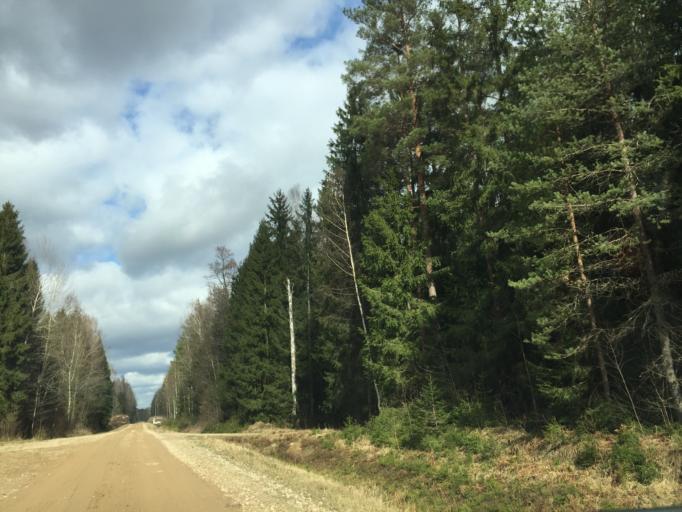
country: LV
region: Vecumnieki
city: Vecumnieki
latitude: 56.5897
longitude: 24.6418
